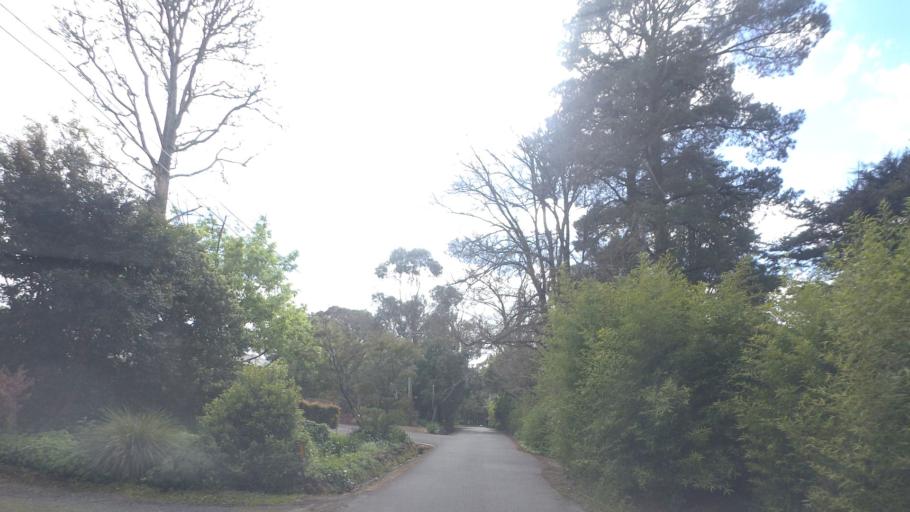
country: AU
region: Victoria
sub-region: Maroondah
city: Croydon South
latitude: -37.8041
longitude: 145.2618
